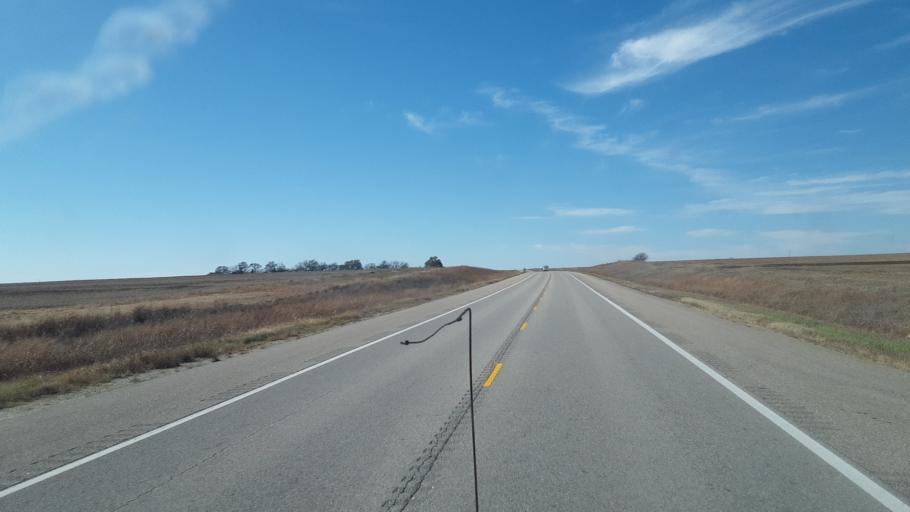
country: US
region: Kansas
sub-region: McPherson County
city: Inman
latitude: 38.3771
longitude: -97.8558
